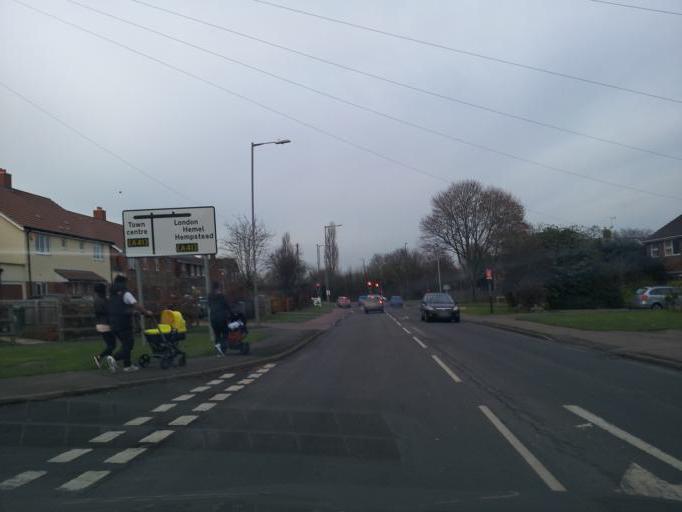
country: GB
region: England
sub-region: Buckinghamshire
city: Weston Turville
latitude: 51.8104
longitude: -0.7757
